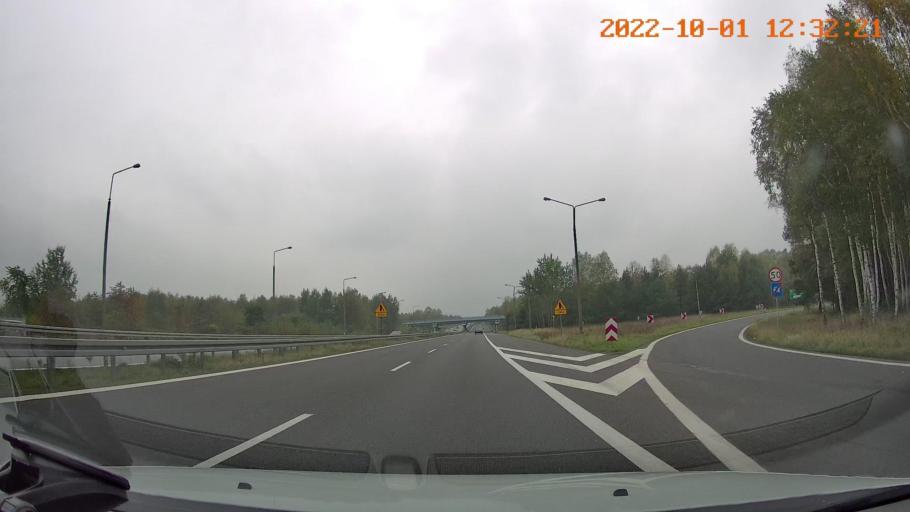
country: PL
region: Silesian Voivodeship
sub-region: Powiat bierunsko-ledzinski
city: Ledziny
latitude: 50.1567
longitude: 19.1421
